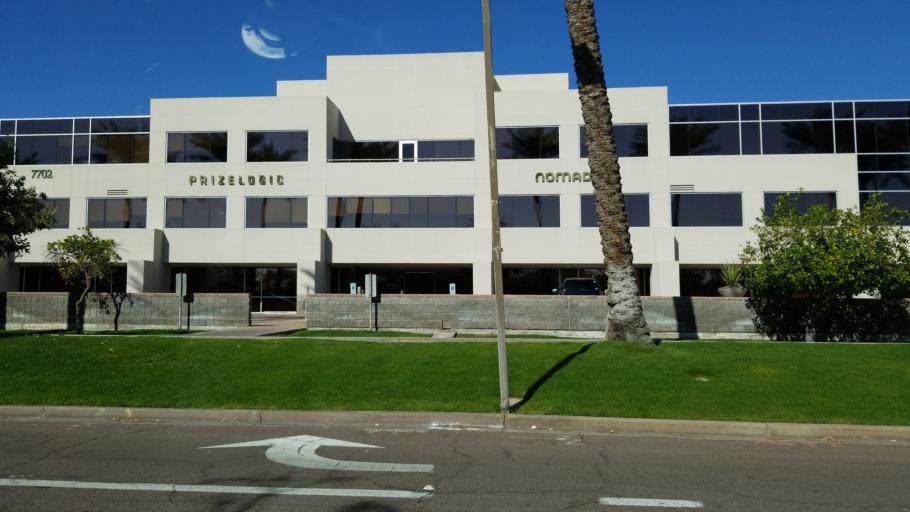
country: US
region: Arizona
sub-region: Maricopa County
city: Paradise Valley
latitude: 33.5647
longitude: -111.9166
